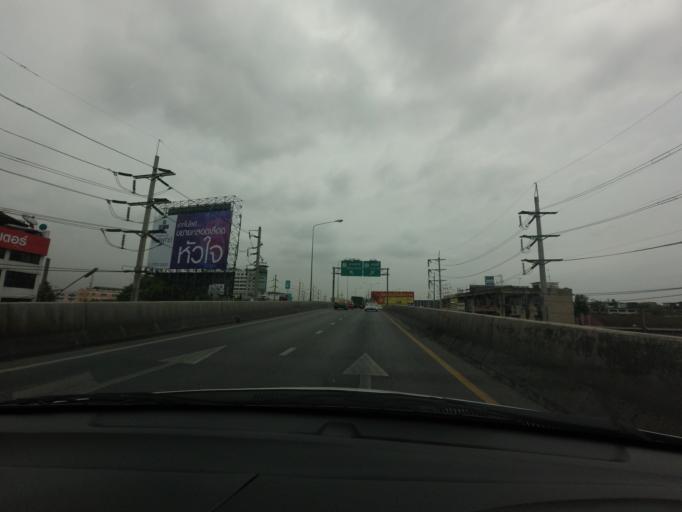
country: TH
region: Bangkok
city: Min Buri
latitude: 13.8134
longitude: 100.7185
